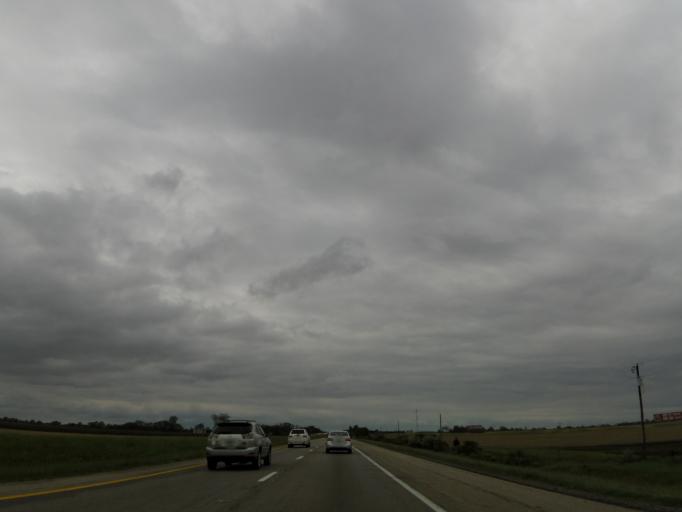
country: US
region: Ohio
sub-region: Madison County
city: Mount Sterling
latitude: 39.7980
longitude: -83.2195
